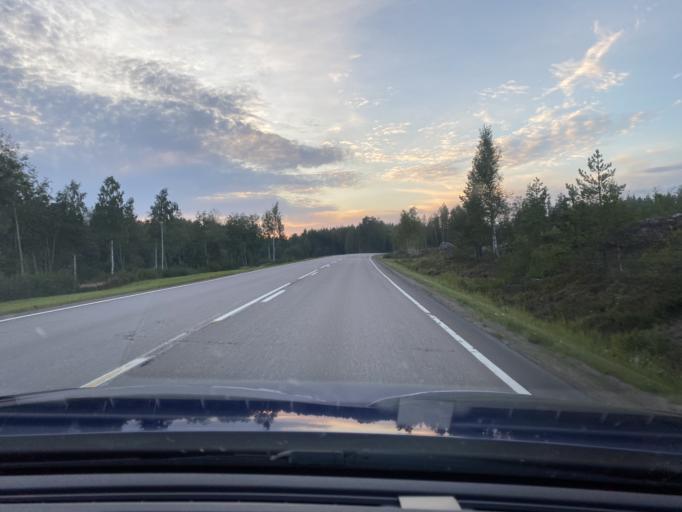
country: FI
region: Satakunta
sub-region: Pohjois-Satakunta
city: Honkajoki
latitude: 61.9414
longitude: 22.2351
